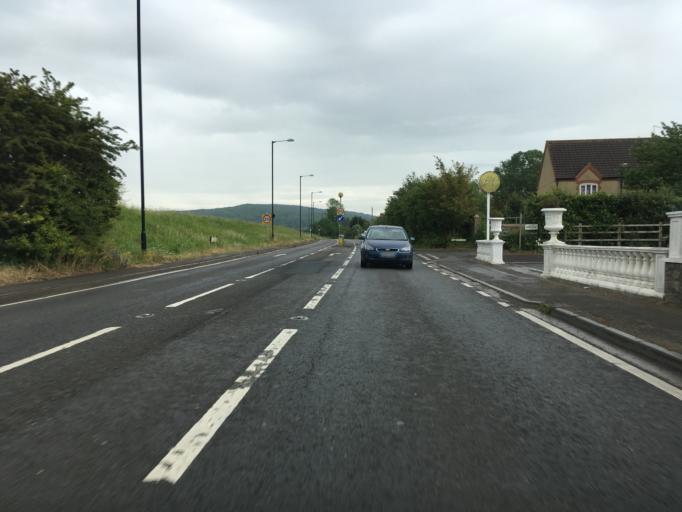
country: GB
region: England
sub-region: North Somerset
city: Congresbury
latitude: 51.3718
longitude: -2.8200
